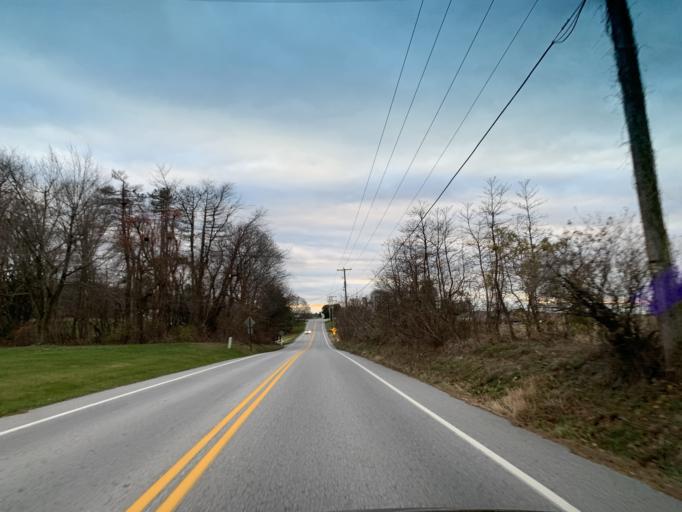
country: US
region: Pennsylvania
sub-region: York County
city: Stewartstown
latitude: 39.7825
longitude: -76.6304
